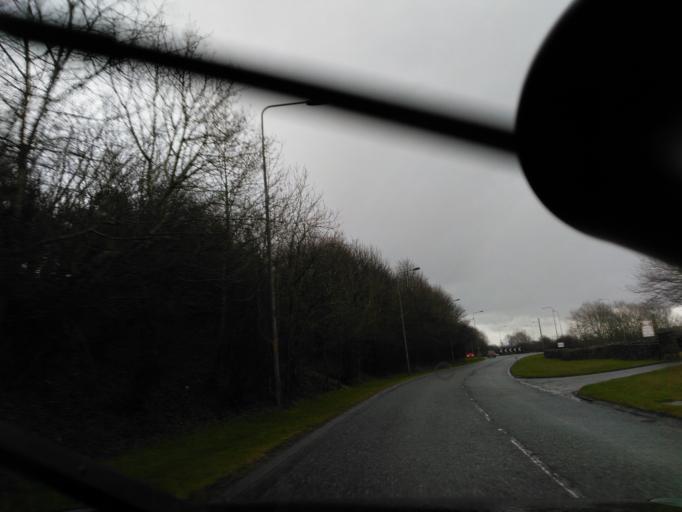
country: GB
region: England
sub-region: North Yorkshire
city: Embsay
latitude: 53.9698
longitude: -1.9838
